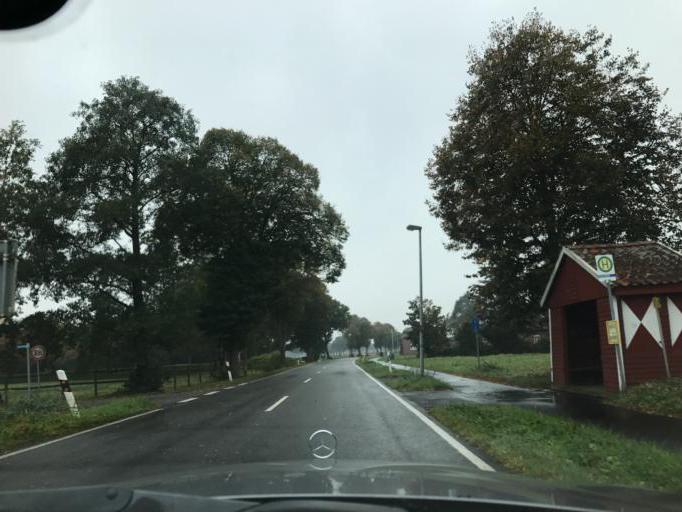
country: DE
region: Lower Saxony
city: Papenburg
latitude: 53.0896
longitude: 7.3702
